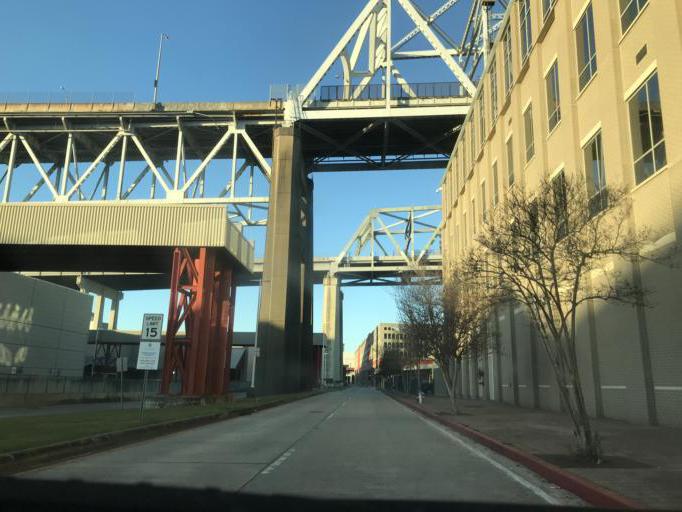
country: US
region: Louisiana
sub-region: Orleans Parish
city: New Orleans
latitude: 29.9369
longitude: -90.0617
